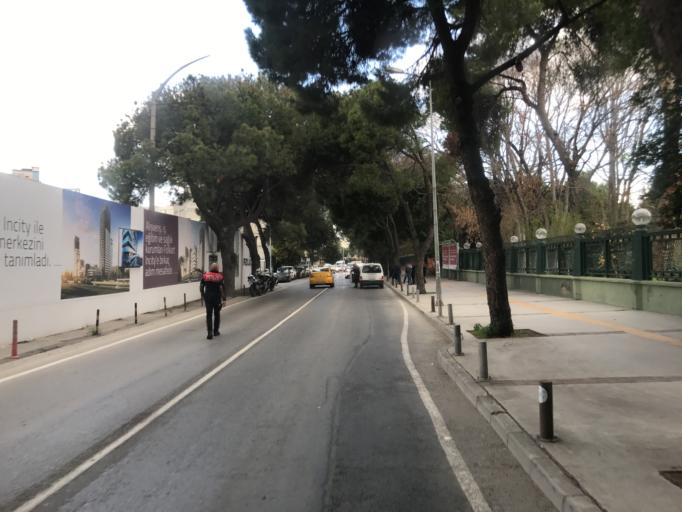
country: TR
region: Izmir
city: Izmir
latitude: 38.4256
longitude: 27.1421
